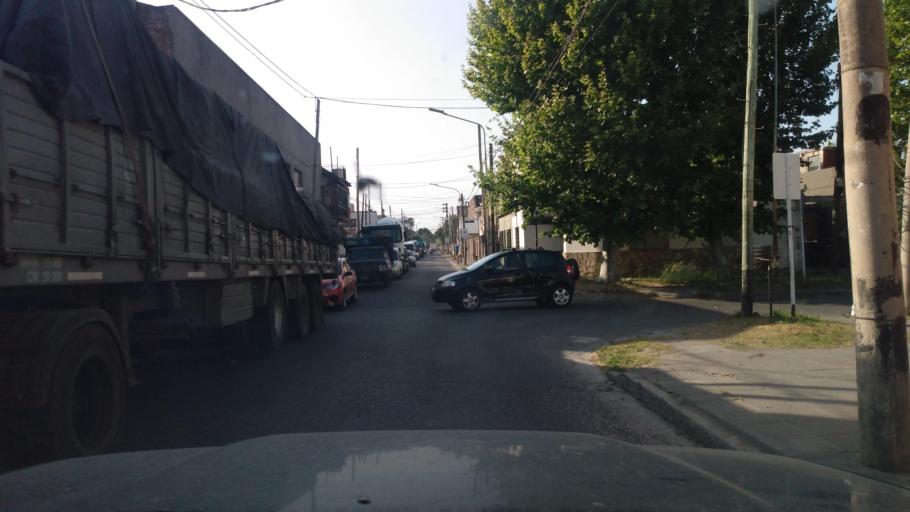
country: AR
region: Buenos Aires
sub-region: Partido de Moron
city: Moron
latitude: -34.6483
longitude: -58.6075
